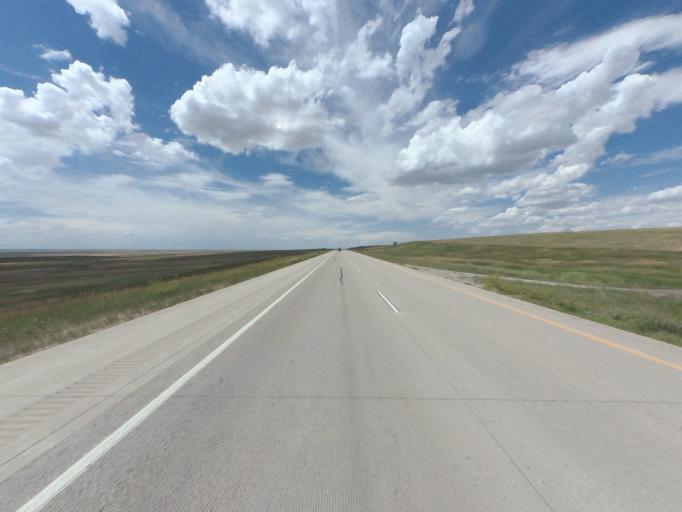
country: US
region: Colorado
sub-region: Lincoln County
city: Limon
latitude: 39.3813
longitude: -103.8889
